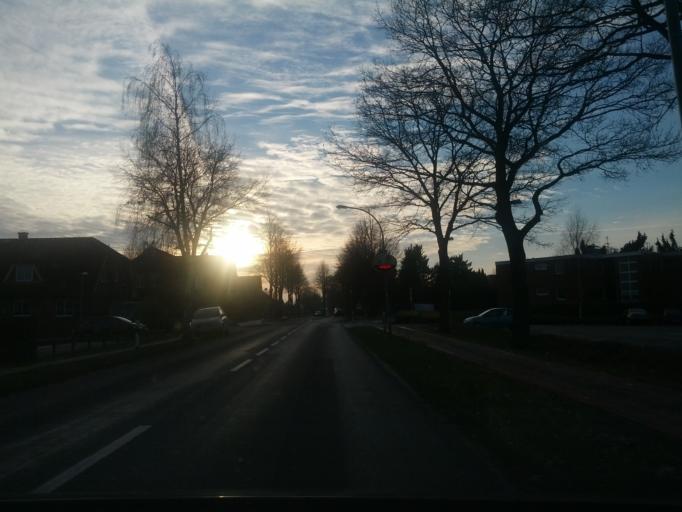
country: DE
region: Lower Saxony
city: Apensen
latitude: 53.4418
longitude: 9.6292
